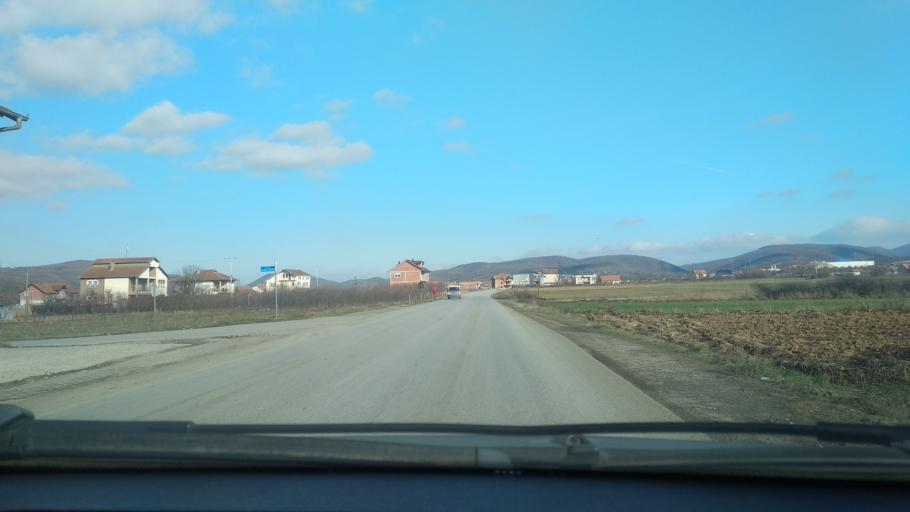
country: XK
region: Pristina
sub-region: Komuna e Obiliqit
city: Obiliq
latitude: 42.7399
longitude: 21.1219
